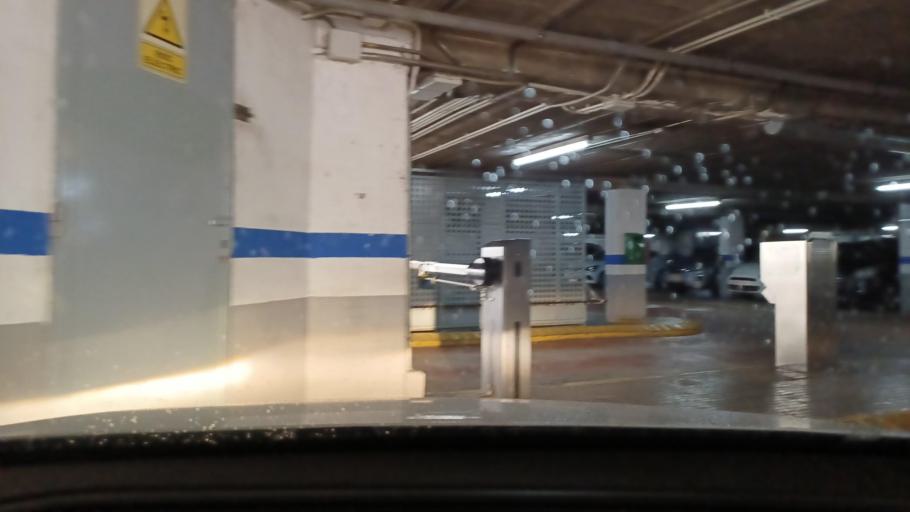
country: ES
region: Catalonia
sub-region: Provincia de Tarragona
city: Tortosa
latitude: 40.8097
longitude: 0.5211
